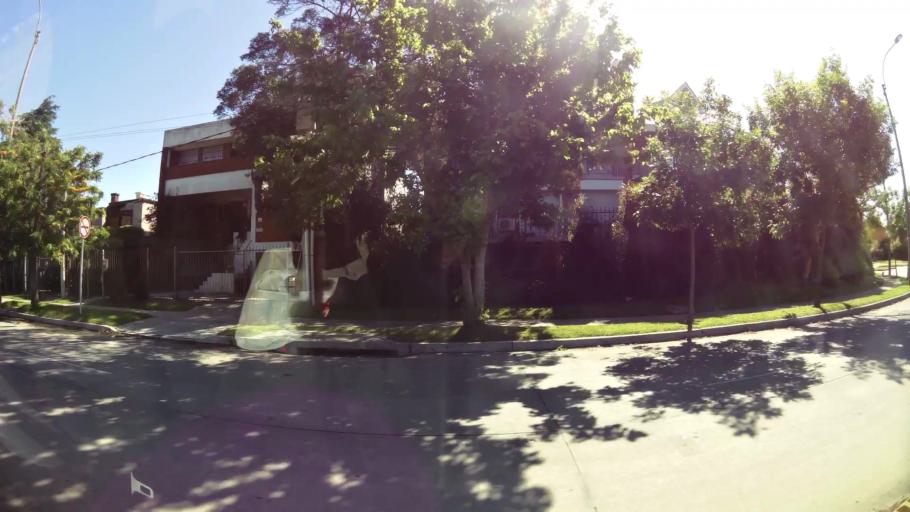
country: UY
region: Canelones
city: Barra de Carrasco
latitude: -34.8774
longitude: -56.0377
